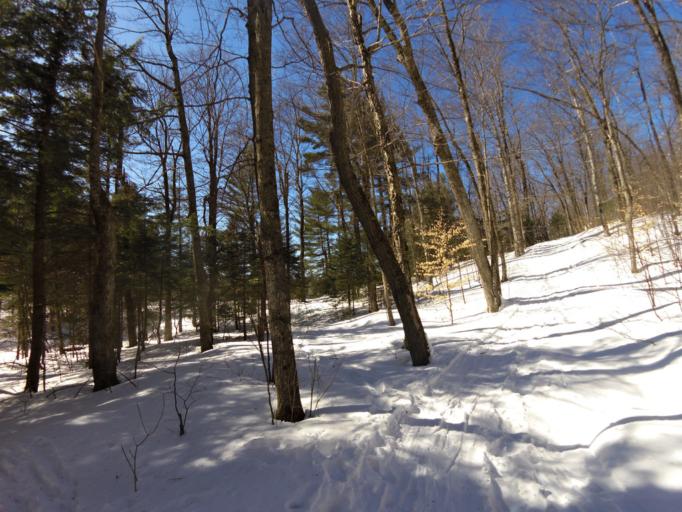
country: CA
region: Quebec
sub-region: Outaouais
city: Wakefield
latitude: 45.5091
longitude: -75.8618
